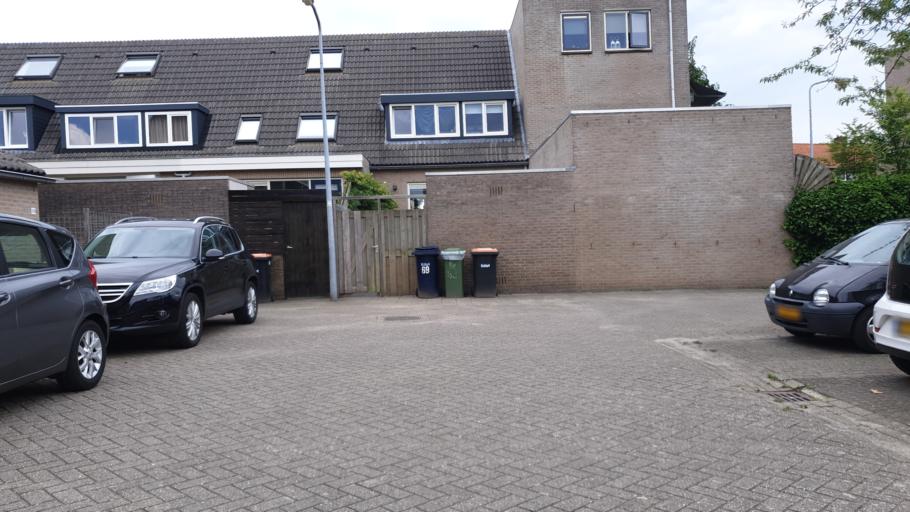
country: NL
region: Utrecht
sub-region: Gemeente Zeist
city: Zeist
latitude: 52.0894
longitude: 5.2356
